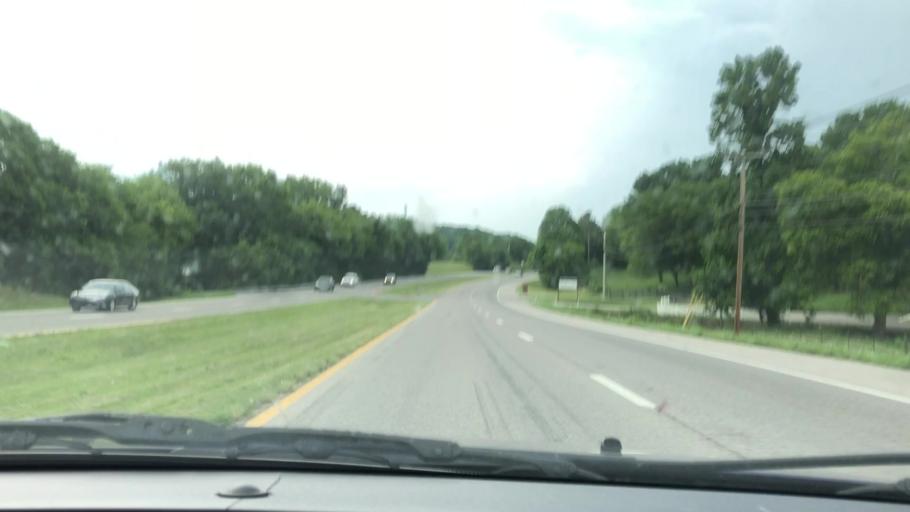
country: US
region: Tennessee
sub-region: Maury County
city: Columbia
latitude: 35.6769
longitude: -86.9995
